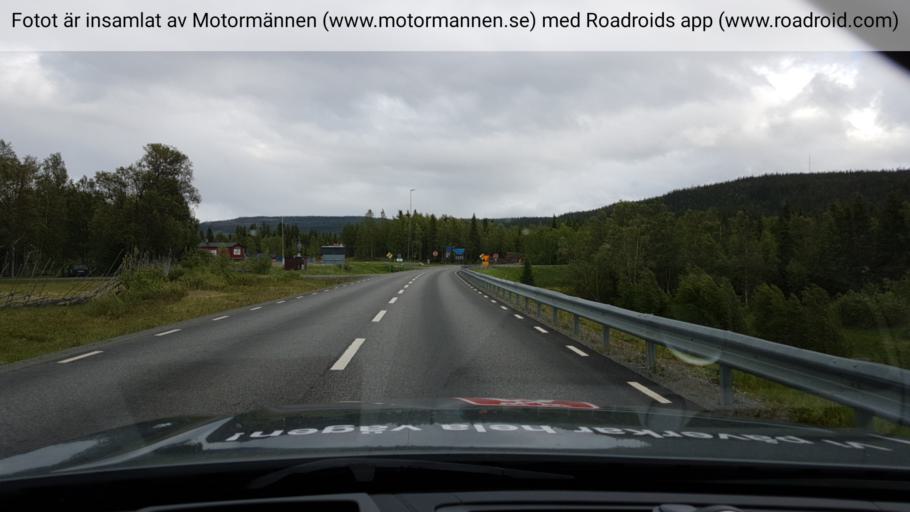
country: SE
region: Jaemtland
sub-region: Are Kommun
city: Are
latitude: 63.4012
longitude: 12.8254
